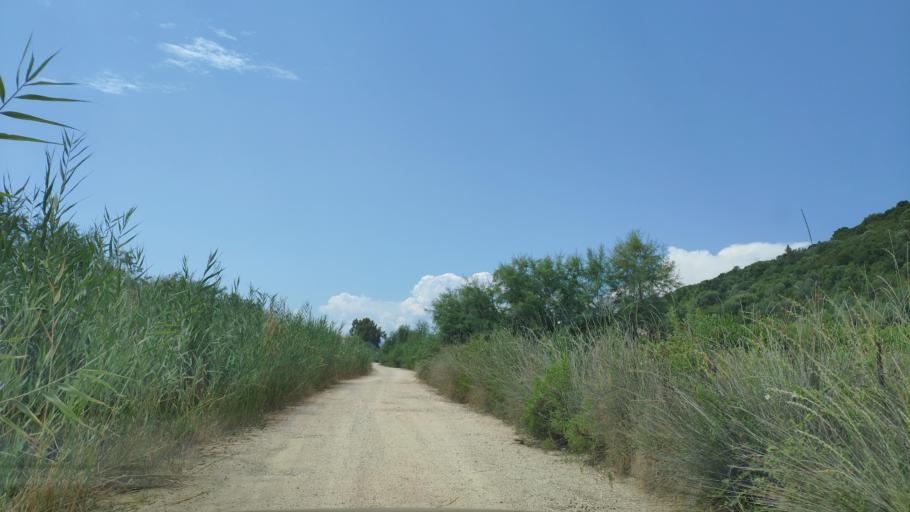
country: GR
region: West Greece
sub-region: Nomos Aitolias kai Akarnanias
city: Menidi
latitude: 39.0506
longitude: 21.1045
